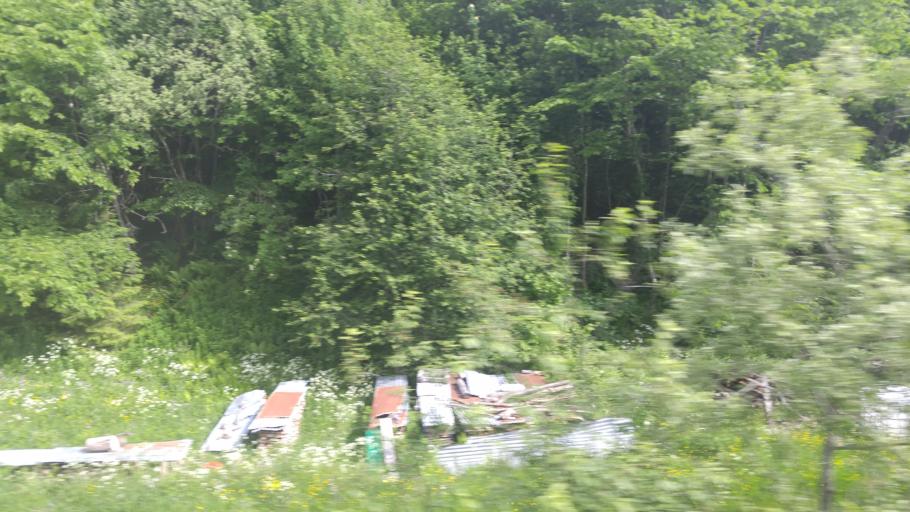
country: NO
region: Sor-Trondelag
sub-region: Midtre Gauldal
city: Storen
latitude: 63.0202
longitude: 10.4269
